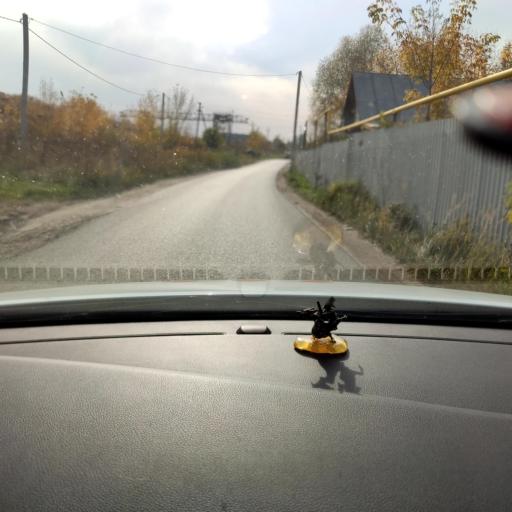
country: RU
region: Tatarstan
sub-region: Gorod Kazan'
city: Kazan
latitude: 55.7550
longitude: 49.1159
